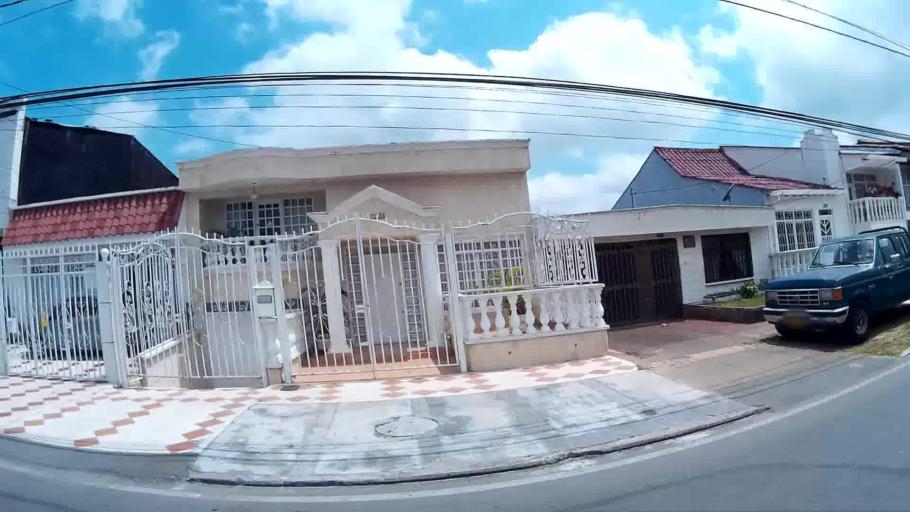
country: CO
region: Quindio
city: Calarca
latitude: 4.5667
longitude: -75.6486
